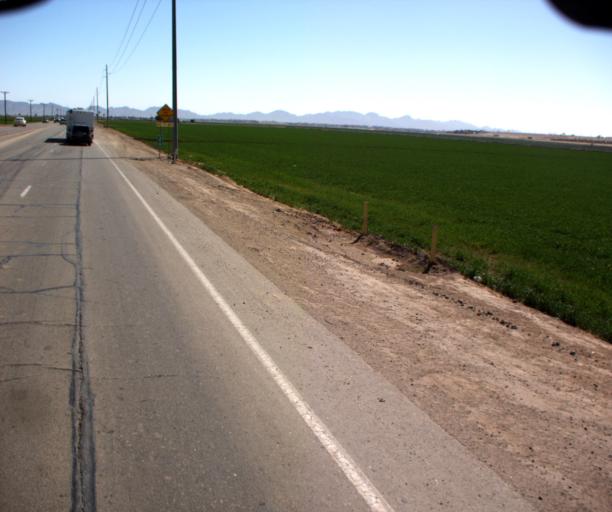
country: US
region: Arizona
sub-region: Yuma County
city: Yuma
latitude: 32.6987
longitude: -114.5794
